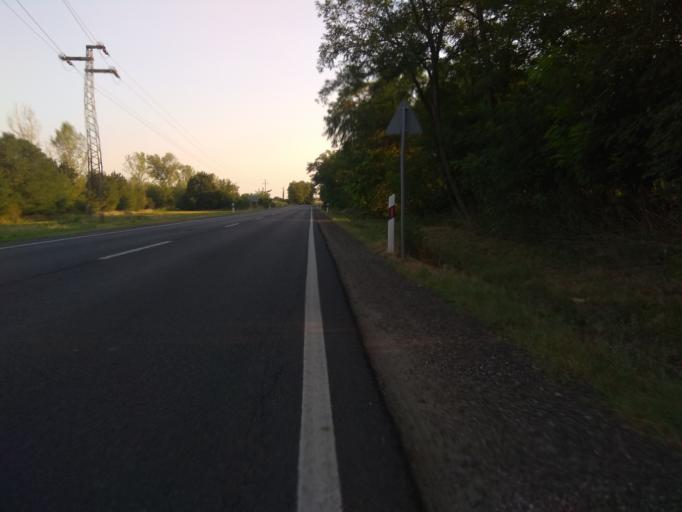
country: HU
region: Borsod-Abauj-Zemplen
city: Emod
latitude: 47.9500
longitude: 20.8328
